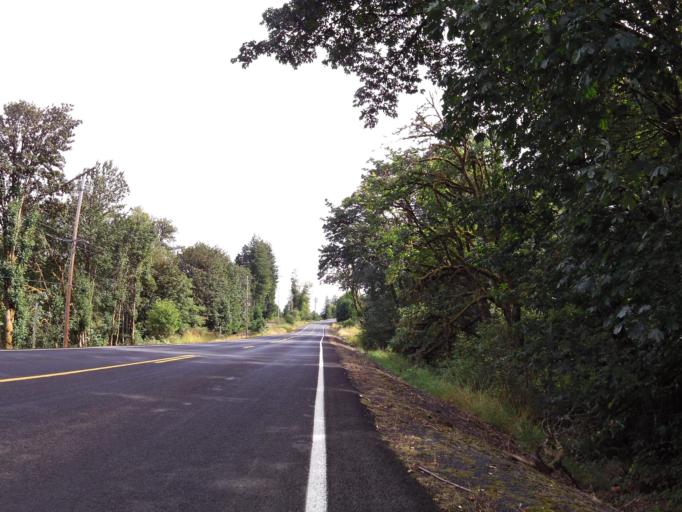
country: US
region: Washington
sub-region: Cowlitz County
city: Castle Rock
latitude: 46.3345
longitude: -122.9332
